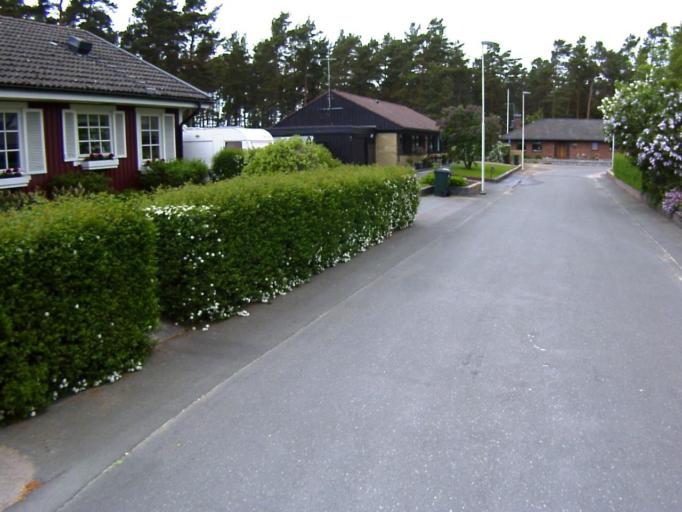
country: SE
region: Skane
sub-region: Kristianstads Kommun
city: Ahus
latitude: 55.9383
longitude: 14.2736
